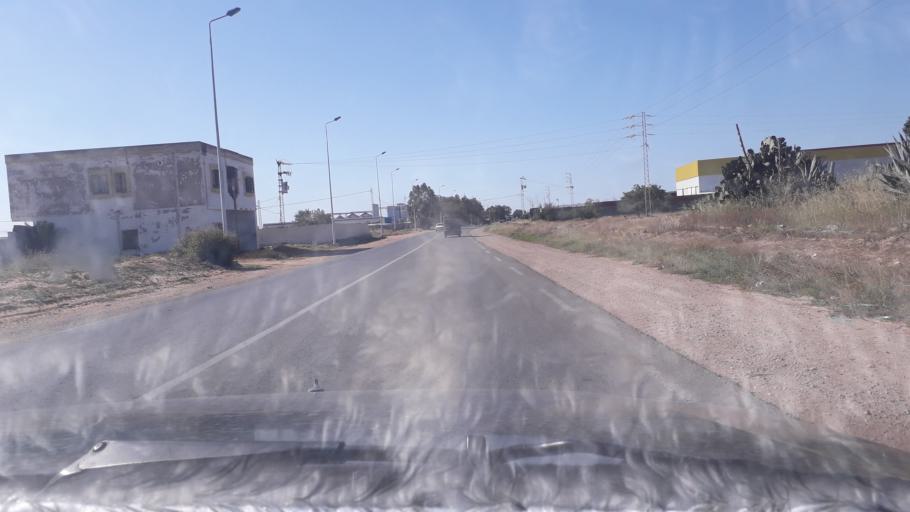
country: TN
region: Safaqis
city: Al Qarmadah
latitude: 34.8700
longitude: 10.7566
